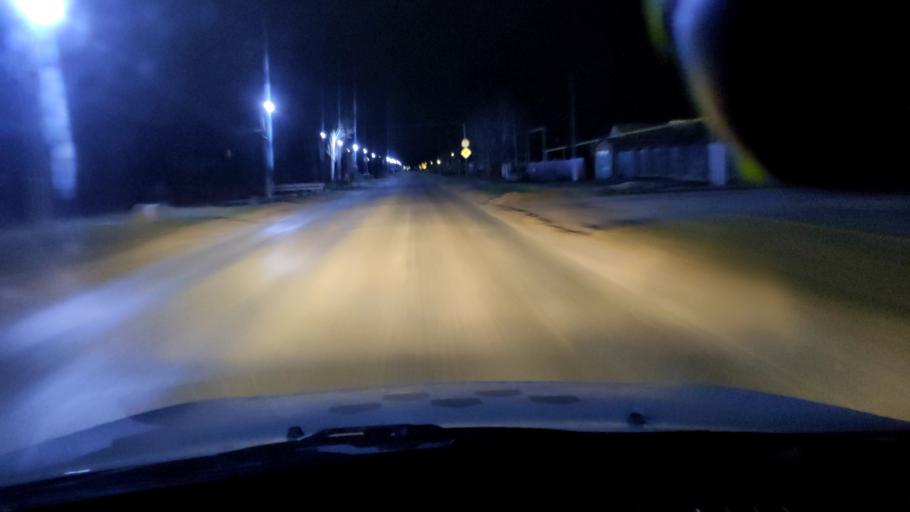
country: RU
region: Samara
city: Podstepki
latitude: 53.6060
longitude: 49.0425
